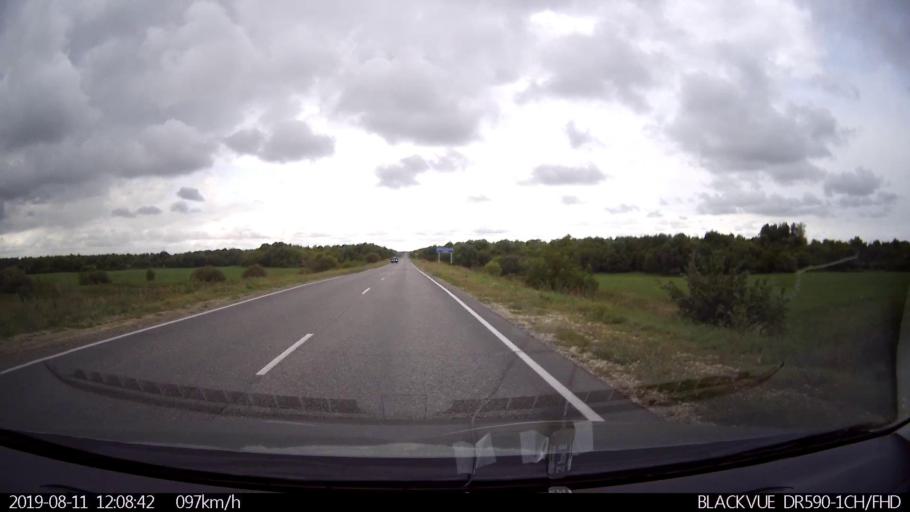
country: RU
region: Ulyanovsk
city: Silikatnyy
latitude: 53.9956
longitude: 48.0645
